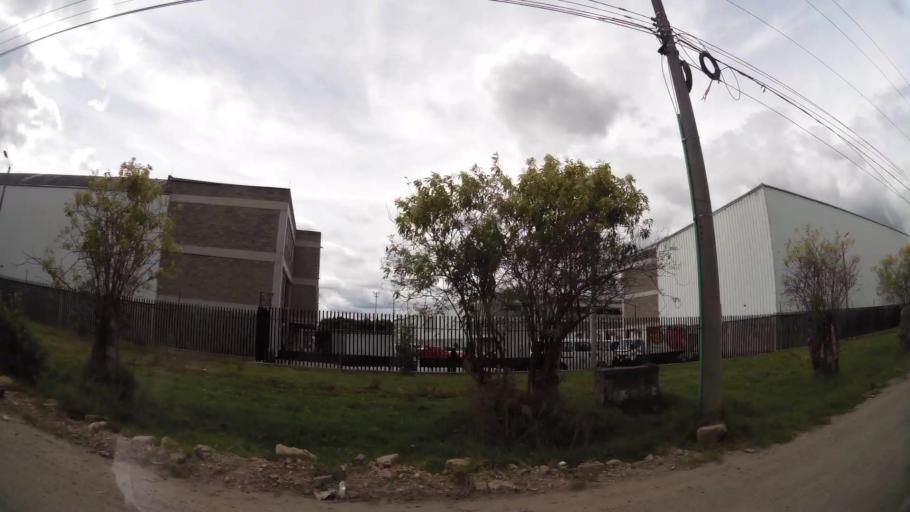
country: CO
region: Cundinamarca
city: Funza
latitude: 4.7340
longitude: -74.1482
